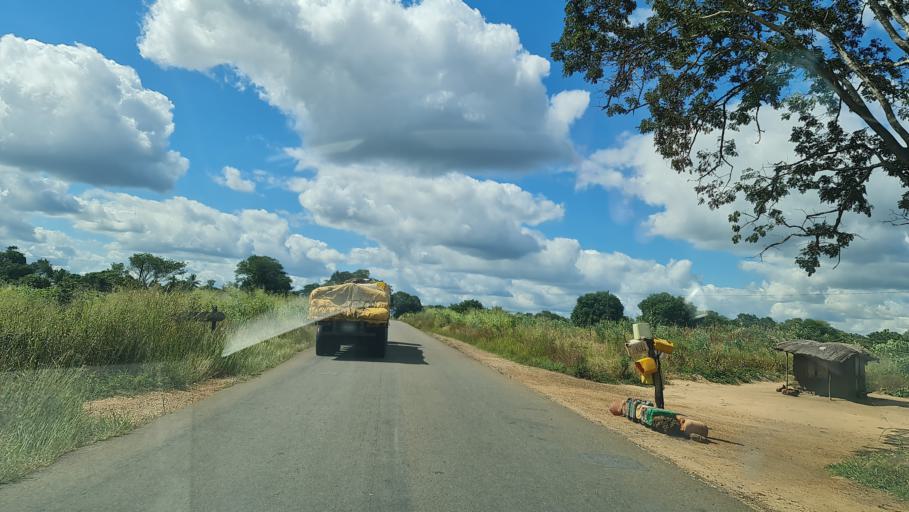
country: MZ
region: Zambezia
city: Quelimane
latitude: -17.5121
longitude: 36.2266
